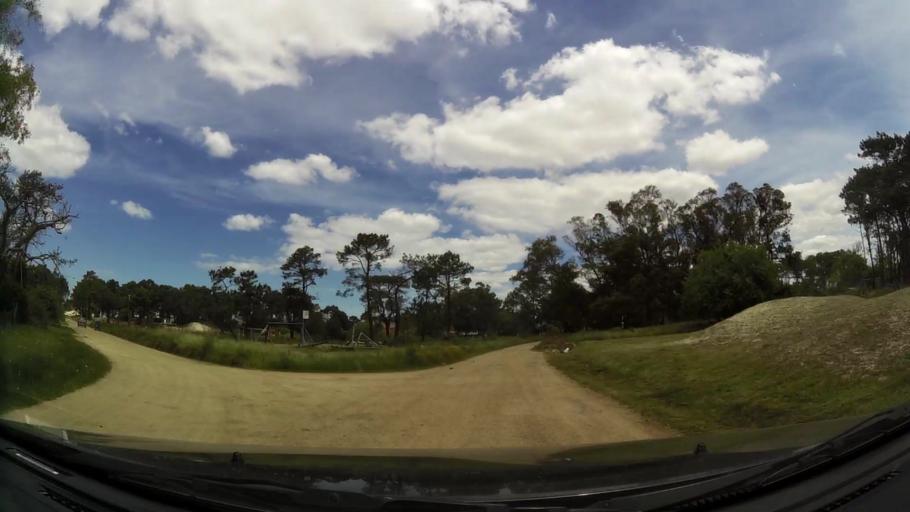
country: UY
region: Canelones
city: Empalme Olmos
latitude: -34.7989
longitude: -55.8904
